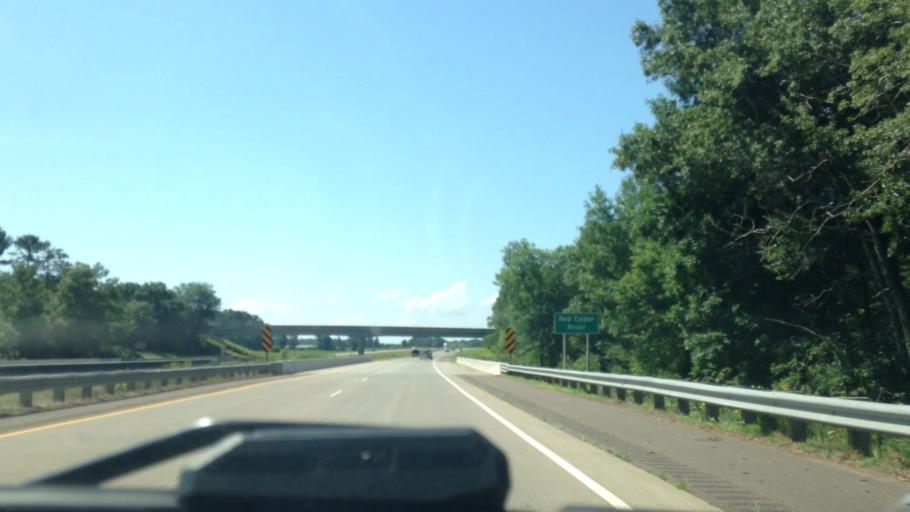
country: US
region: Wisconsin
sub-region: Barron County
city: Cameron
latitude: 45.4469
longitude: -91.7598
